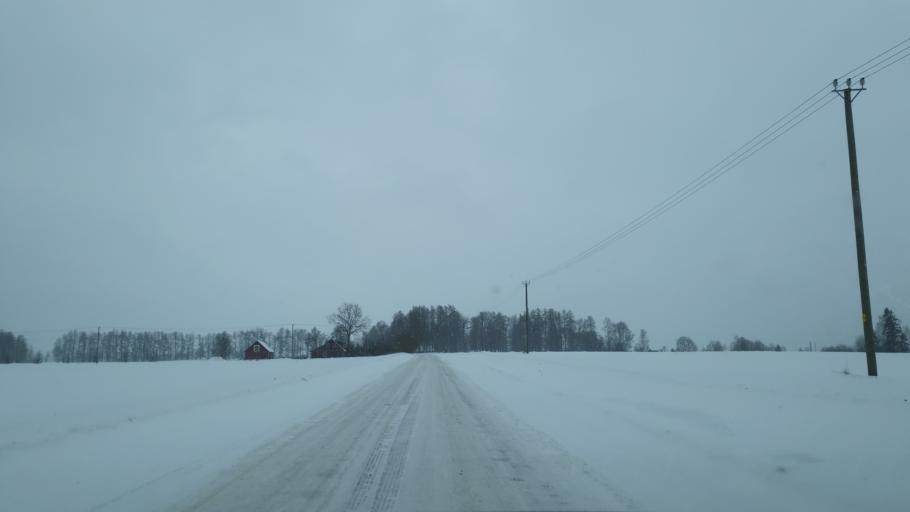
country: EE
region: Tartu
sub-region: Tartu linn
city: Tartu
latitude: 58.5335
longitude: 26.8755
